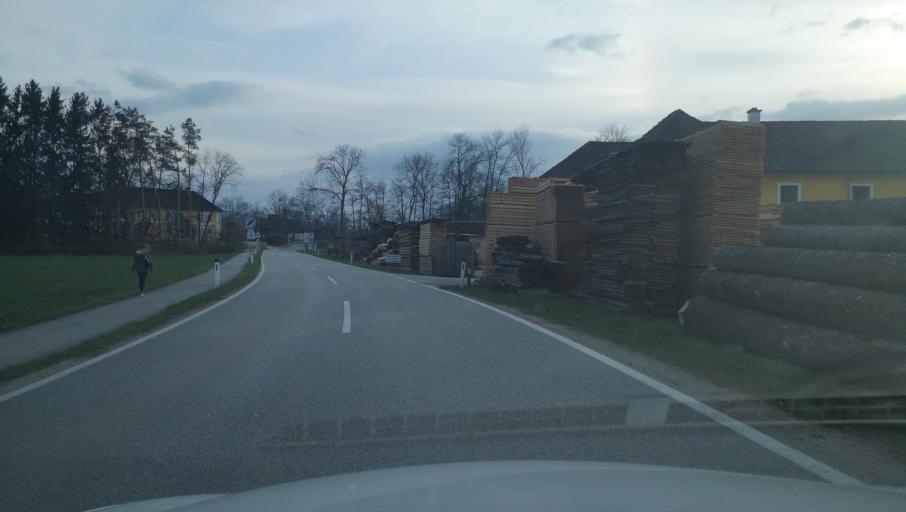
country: AT
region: Lower Austria
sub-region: Politischer Bezirk Amstetten
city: Euratsfeld
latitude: 48.0949
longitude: 14.9275
